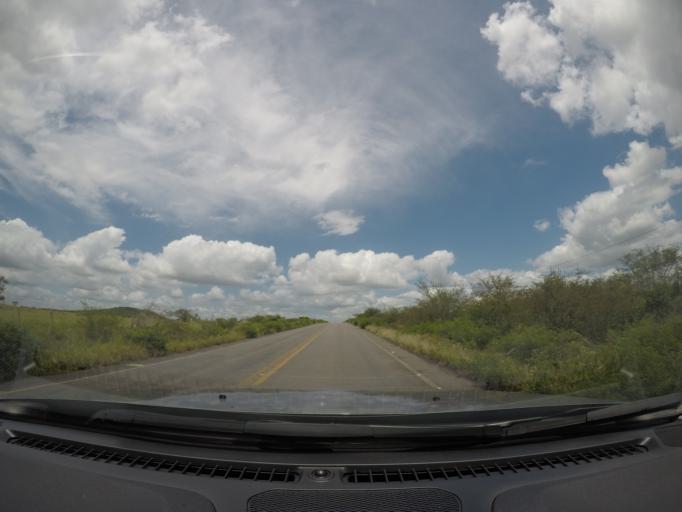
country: BR
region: Bahia
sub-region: Ipira
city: Ipira
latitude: -12.2401
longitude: -39.8004
